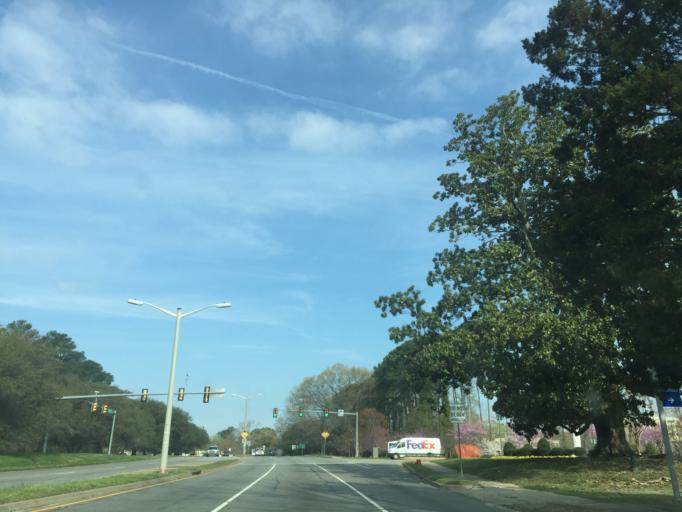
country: US
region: Virginia
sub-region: City of Newport News
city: Newport News
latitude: 37.0588
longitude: -76.4838
